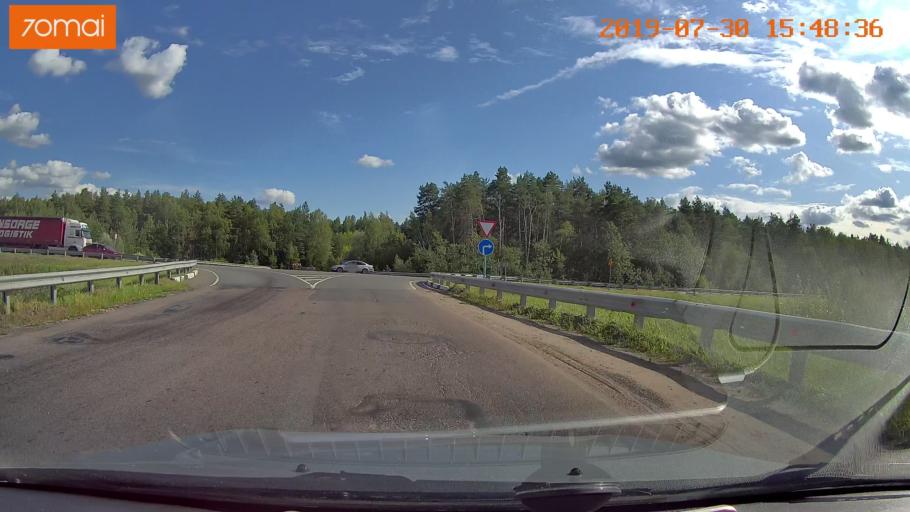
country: RU
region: Moskovskaya
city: Voskresensk
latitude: 55.3414
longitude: 38.6781
